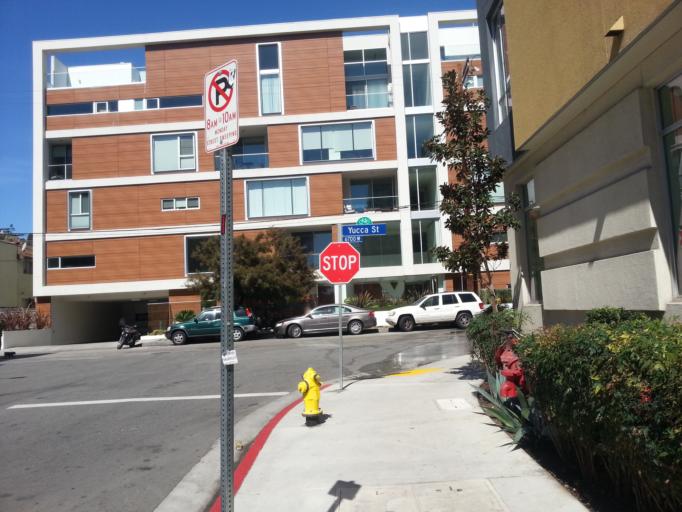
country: US
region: California
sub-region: Los Angeles County
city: Hollywood
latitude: 34.1030
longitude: -118.3375
